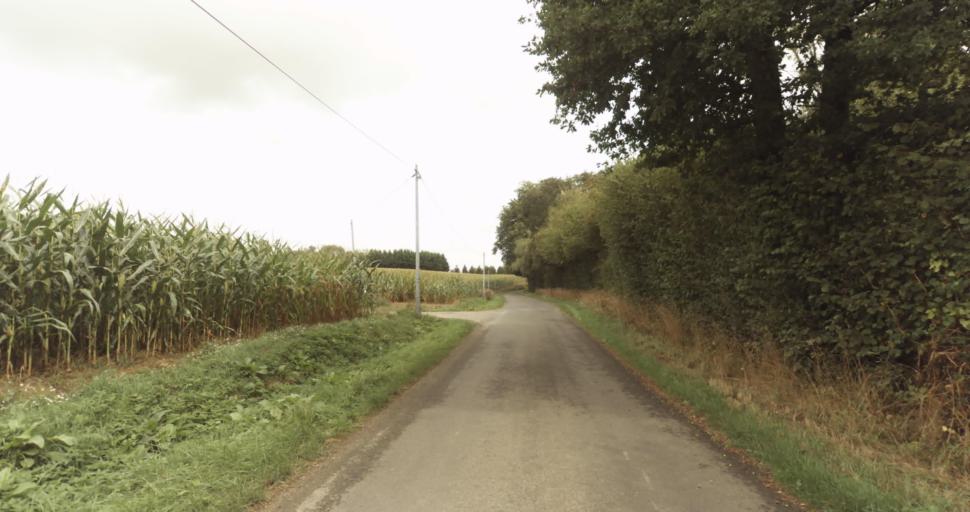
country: FR
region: Lower Normandy
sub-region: Departement de l'Orne
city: Gace
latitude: 48.8260
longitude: 0.3705
